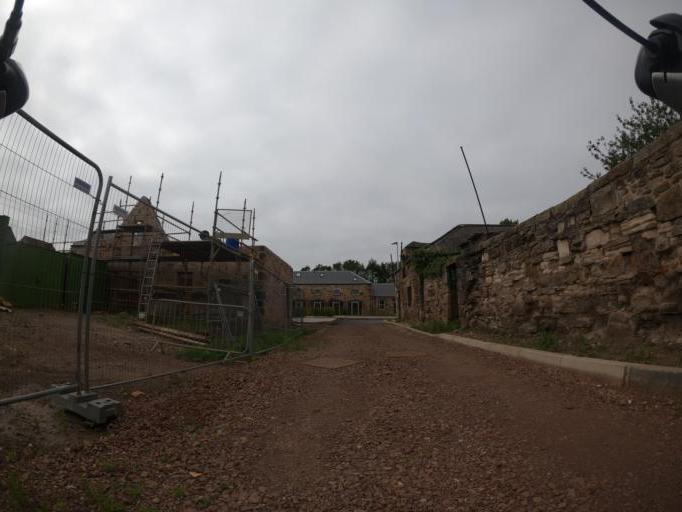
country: GB
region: Scotland
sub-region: East Lothian
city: Musselburgh
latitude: 55.9396
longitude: -3.0938
